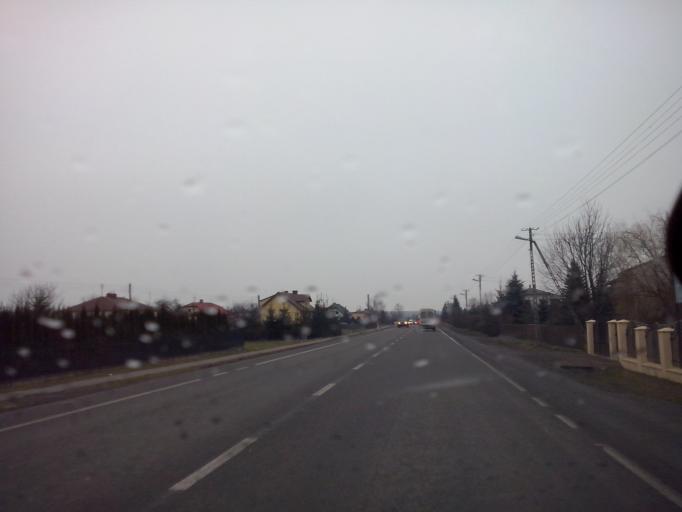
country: PL
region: Lublin Voivodeship
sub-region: Powiat zamojski
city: Michalow
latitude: 50.7164
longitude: 23.0349
